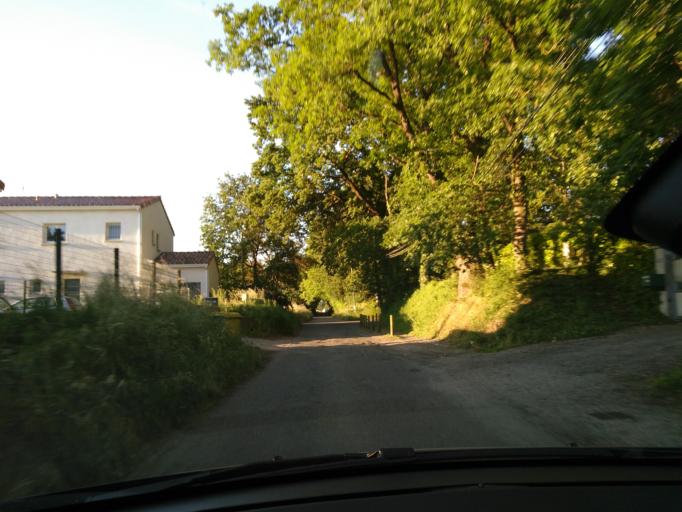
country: FR
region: Midi-Pyrenees
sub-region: Departement de la Haute-Garonne
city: Grenade
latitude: 43.7585
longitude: 1.2981
